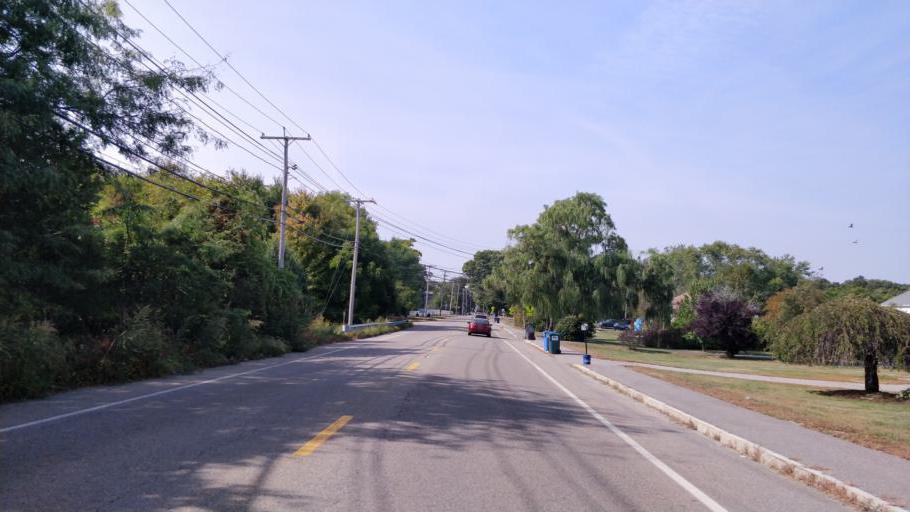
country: US
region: Massachusetts
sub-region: Bristol County
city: Norton
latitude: 41.9556
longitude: -71.2160
